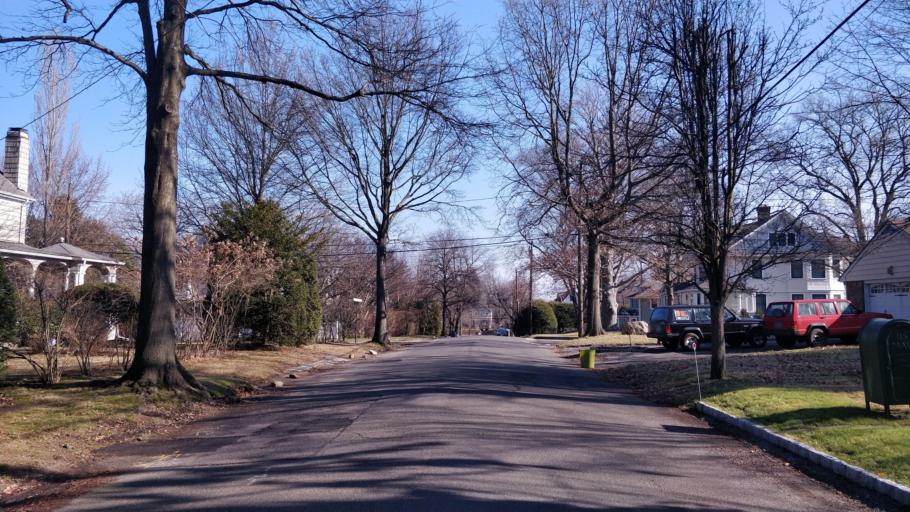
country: US
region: New York
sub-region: Nassau County
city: Sea Cliff
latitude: 40.8456
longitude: -73.6382
